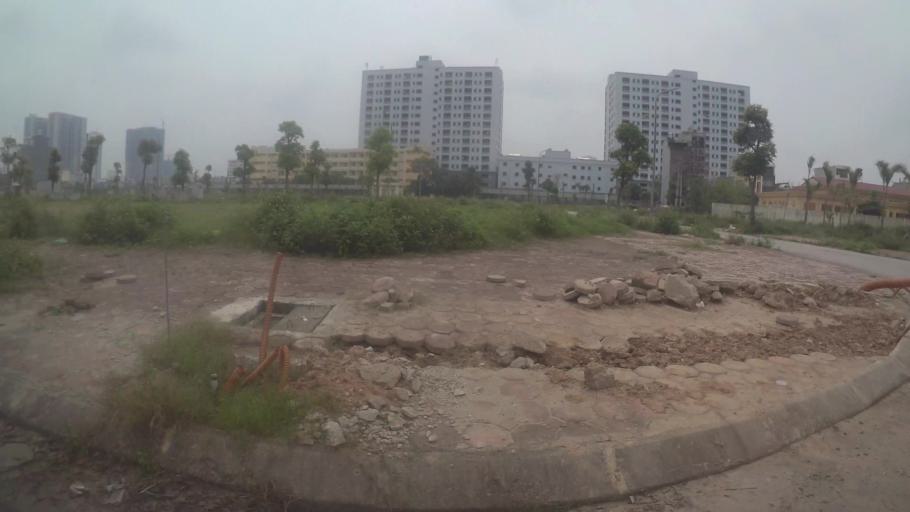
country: VN
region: Ha Noi
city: Ha Dong
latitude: 20.9762
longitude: 105.7680
